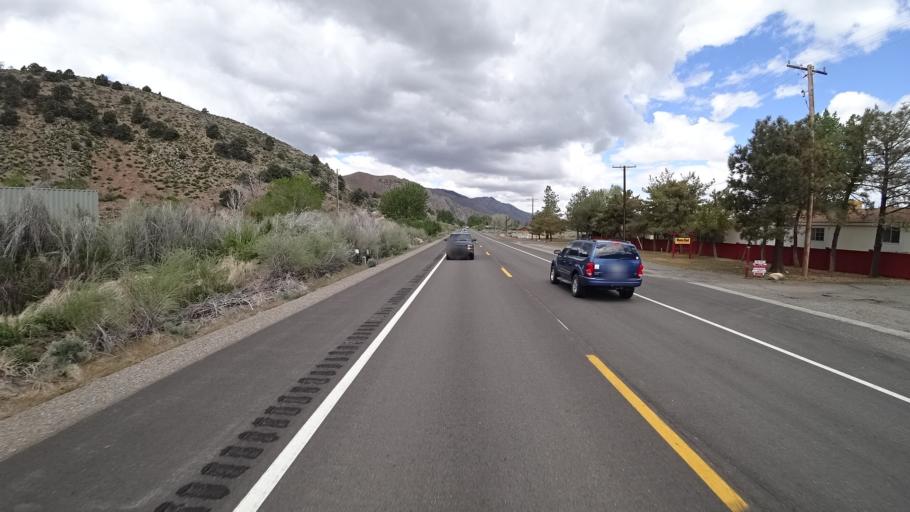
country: US
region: Nevada
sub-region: Lyon County
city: Smith Valley
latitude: 38.5326
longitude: -119.4914
